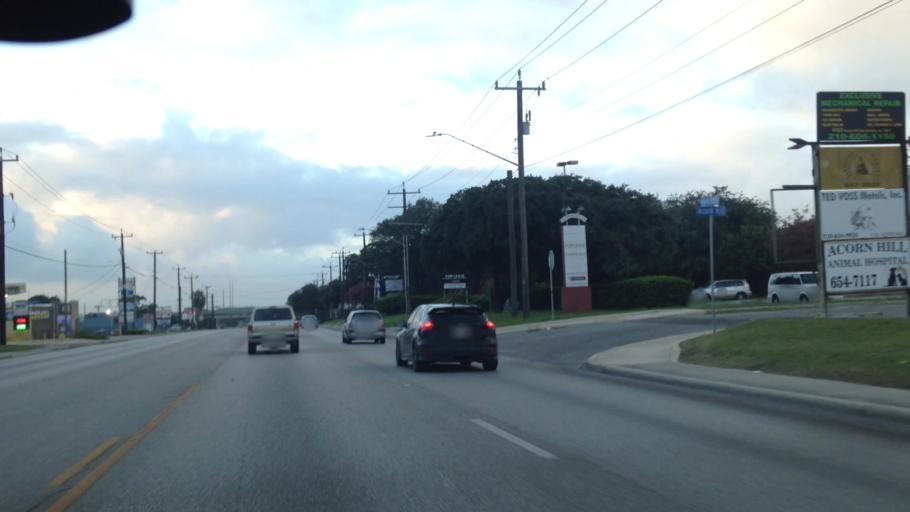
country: US
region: Texas
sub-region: Bexar County
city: Windcrest
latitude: 29.5391
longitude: -98.4111
